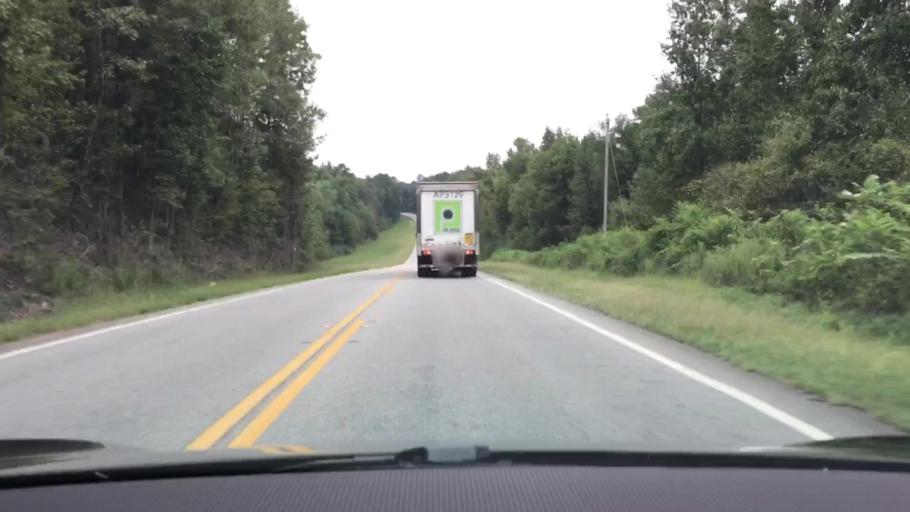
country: US
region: Georgia
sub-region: Greene County
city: Greensboro
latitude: 33.6891
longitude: -83.2750
